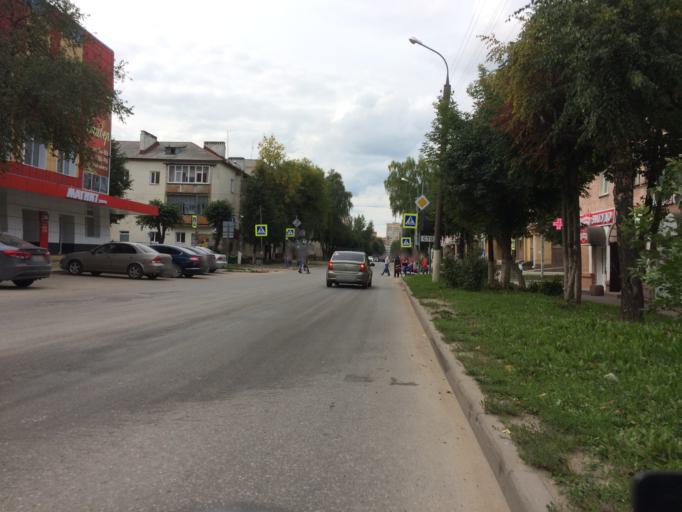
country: RU
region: Mariy-El
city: Yoshkar-Ola
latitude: 56.6353
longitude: 47.8711
